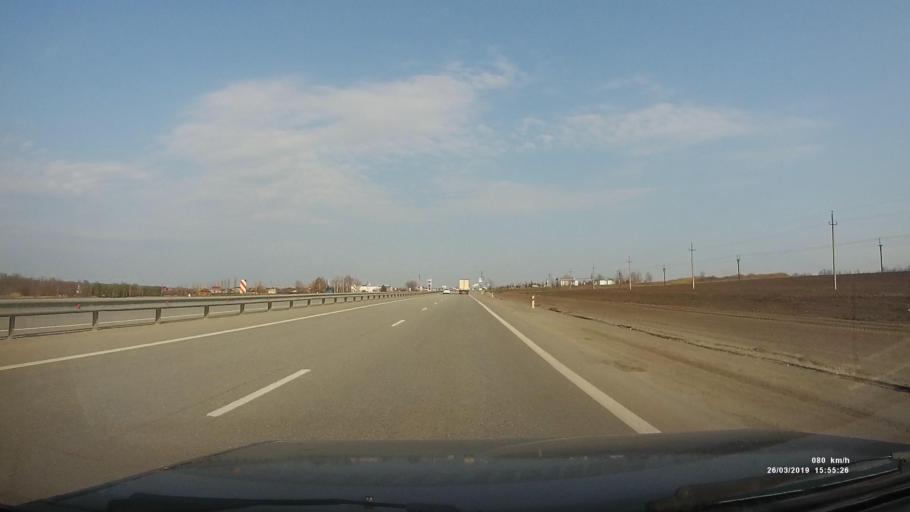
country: RU
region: Rostov
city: Kalinin
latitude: 47.2659
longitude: 39.5761
